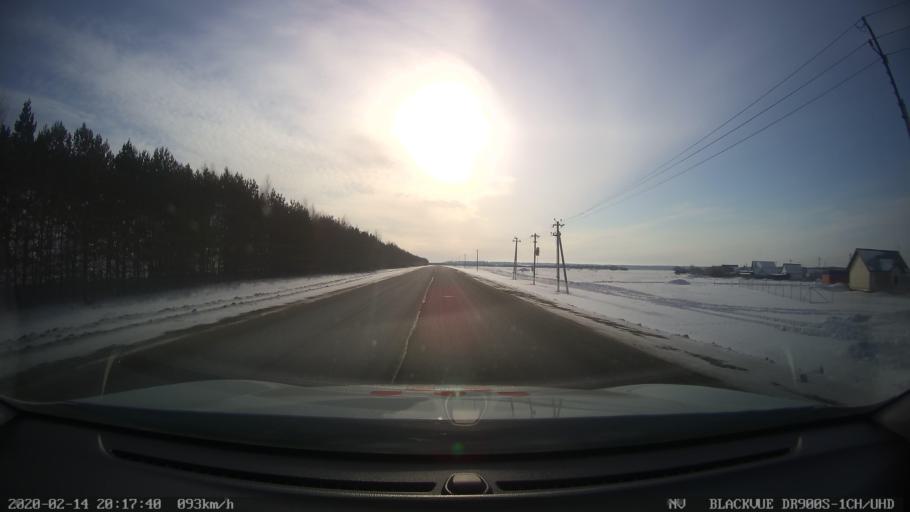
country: RU
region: Tatarstan
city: Verkhniy Uslon
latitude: 55.5969
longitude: 48.8792
